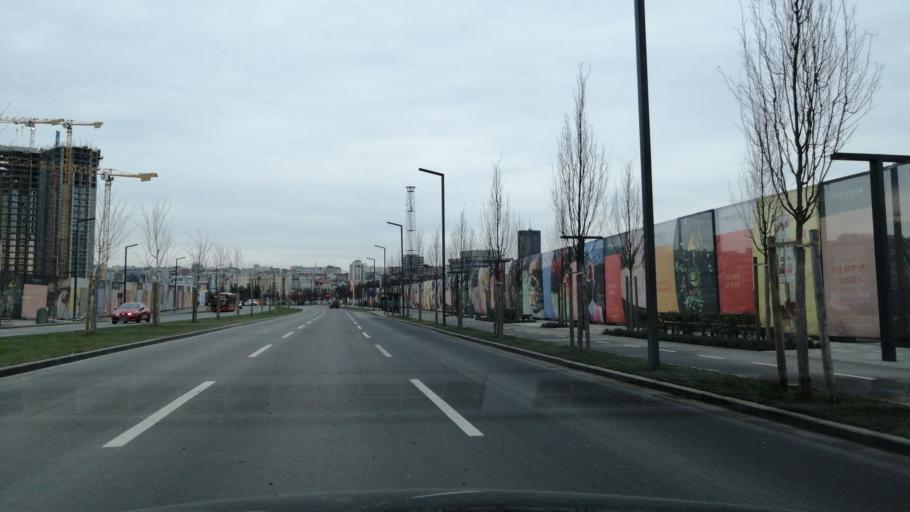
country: RS
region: Central Serbia
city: Belgrade
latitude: 44.8028
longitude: 20.4481
